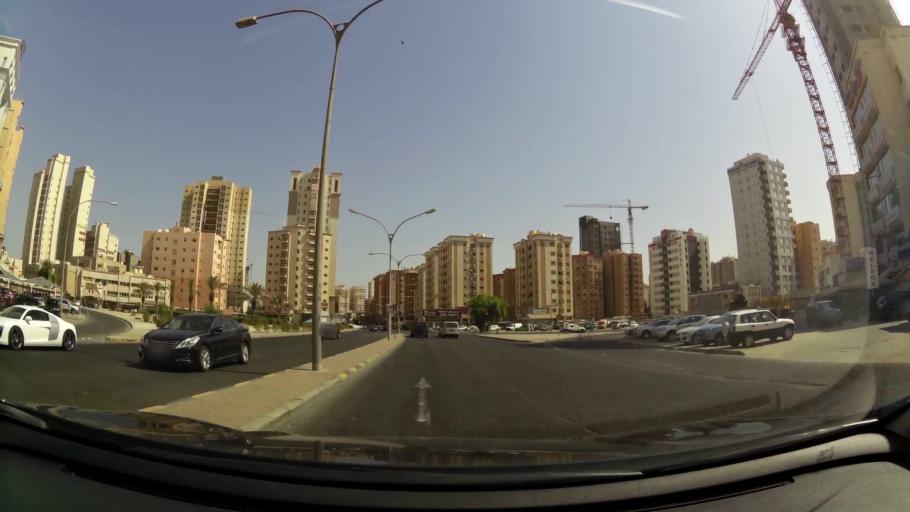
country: KW
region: Muhafazat Hawalli
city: As Salimiyah
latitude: 29.3365
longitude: 48.0527
